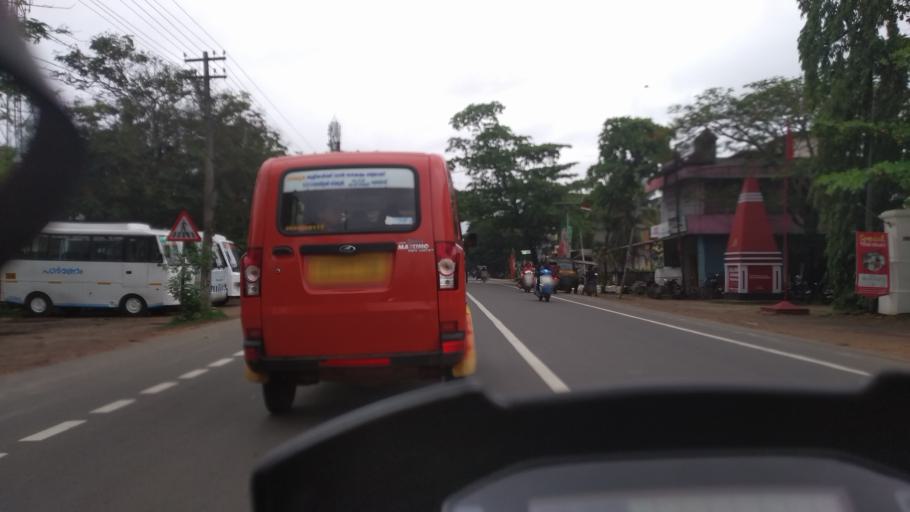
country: IN
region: Kerala
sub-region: Alappuzha
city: Alleppey
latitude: 9.4509
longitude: 76.3417
